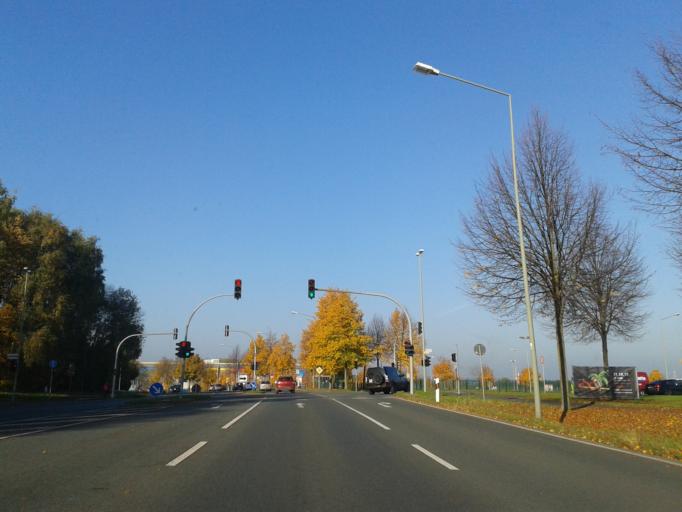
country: DE
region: North Rhine-Westphalia
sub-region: Regierungsbezirk Detmold
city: Paderborn
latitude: 51.7293
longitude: 8.7212
